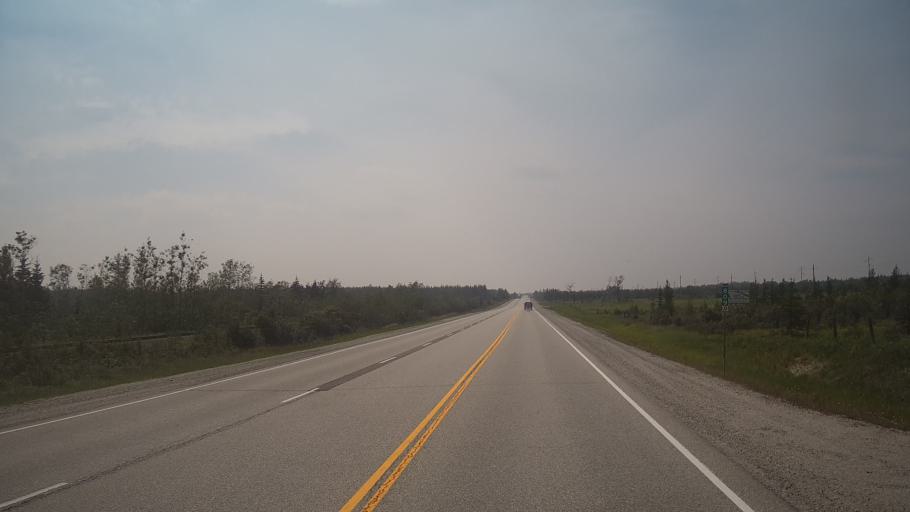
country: CA
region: Ontario
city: Kapuskasing
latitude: 49.3355
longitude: -82.0954
